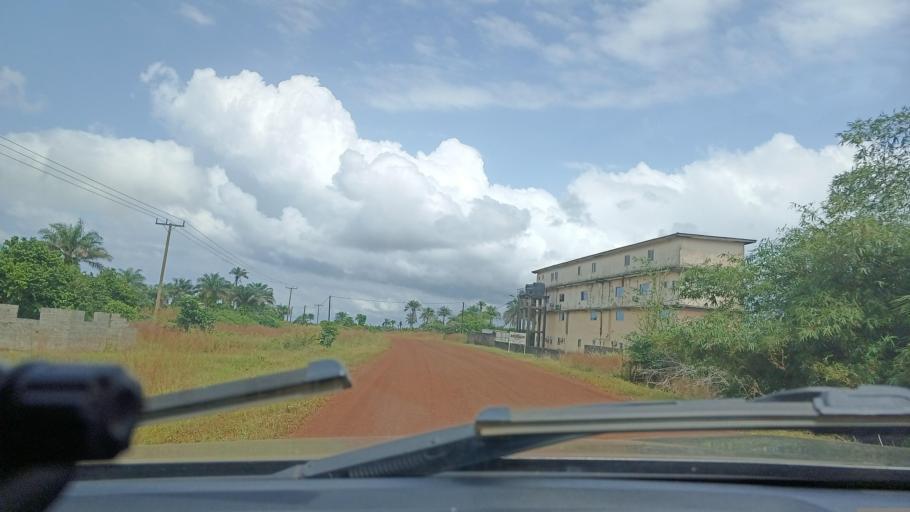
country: LR
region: Grand Cape Mount
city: Robertsport
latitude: 6.7449
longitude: -11.3386
